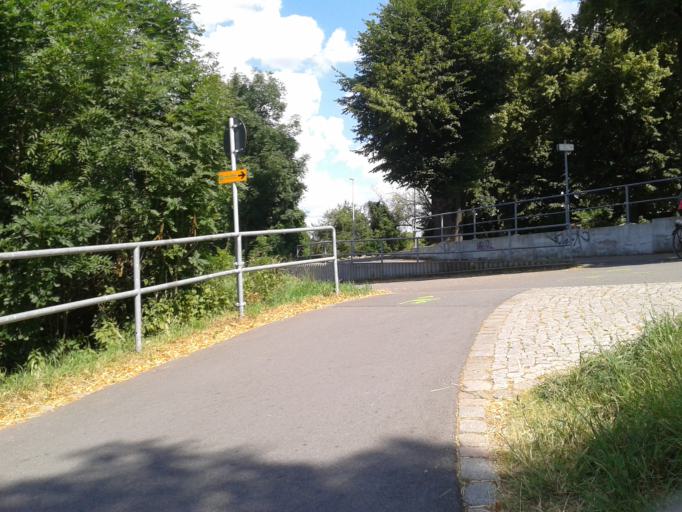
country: DE
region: Saxony
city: Dresden
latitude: 51.0632
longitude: 13.6922
